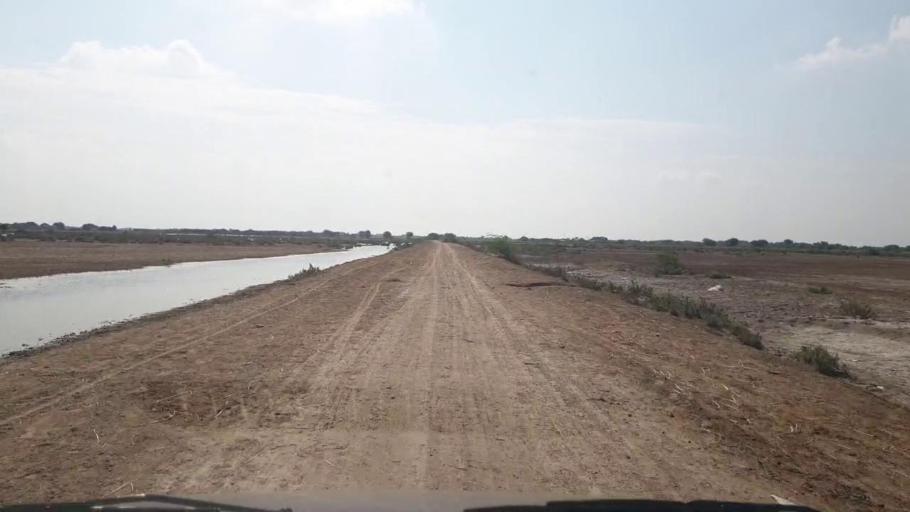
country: PK
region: Sindh
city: Badin
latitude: 24.4916
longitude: 68.6119
